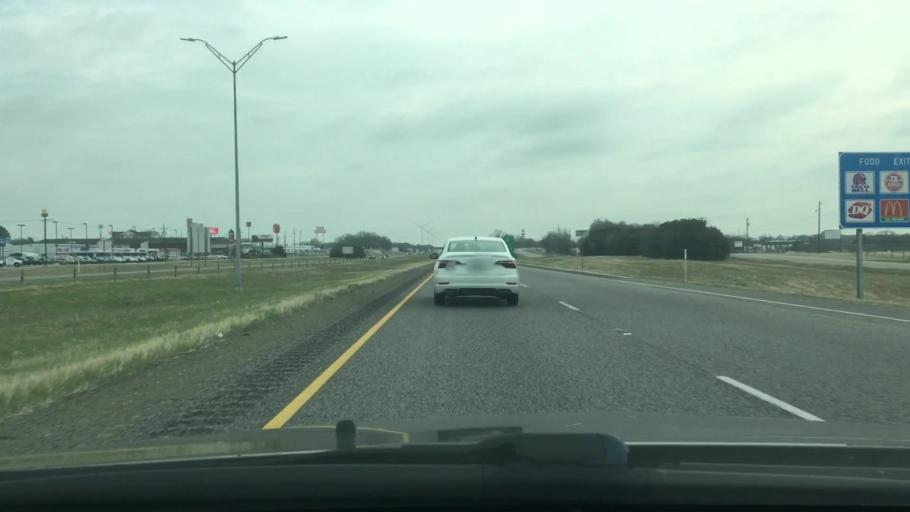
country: US
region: Texas
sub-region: Freestone County
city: Fairfield
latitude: 31.7231
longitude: -96.1793
